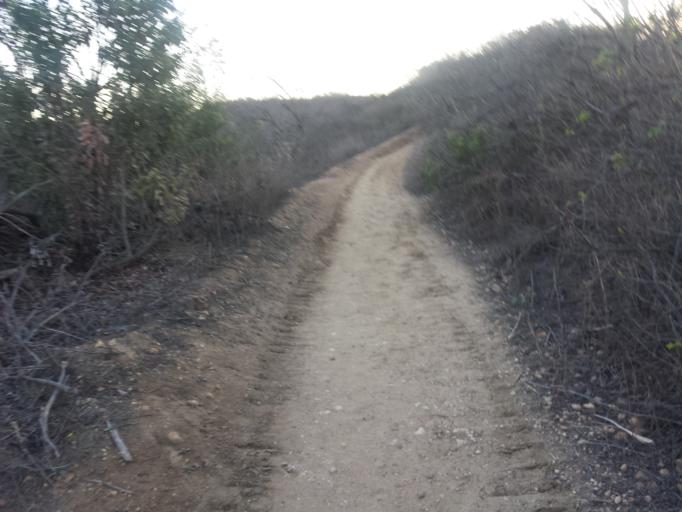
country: US
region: California
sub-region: Los Angeles County
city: Avocado Heights
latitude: 34.0058
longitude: -118.0037
